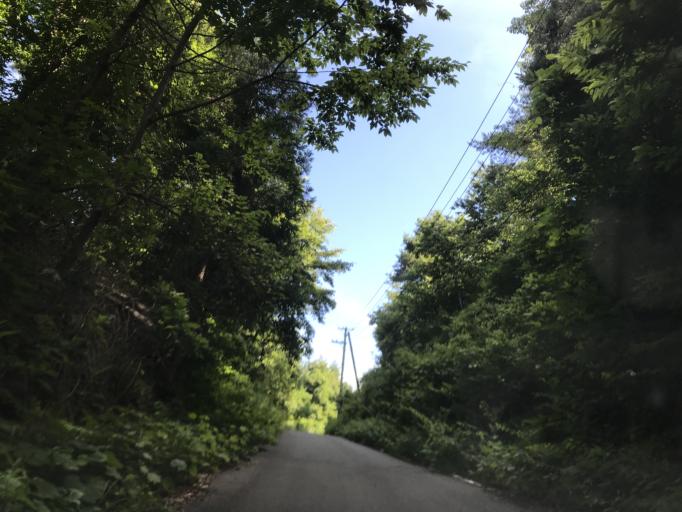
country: JP
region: Iwate
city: Ichinoseki
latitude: 38.8907
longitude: 140.9043
